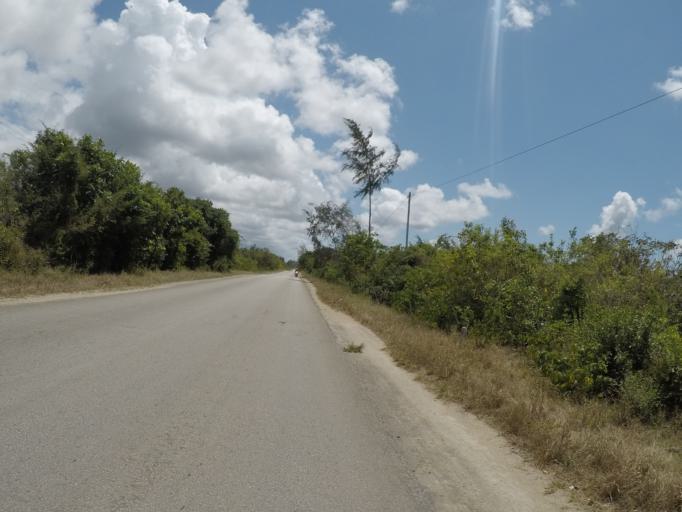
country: TZ
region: Zanzibar Central/South
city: Nganane
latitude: -6.2773
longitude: 39.4319
